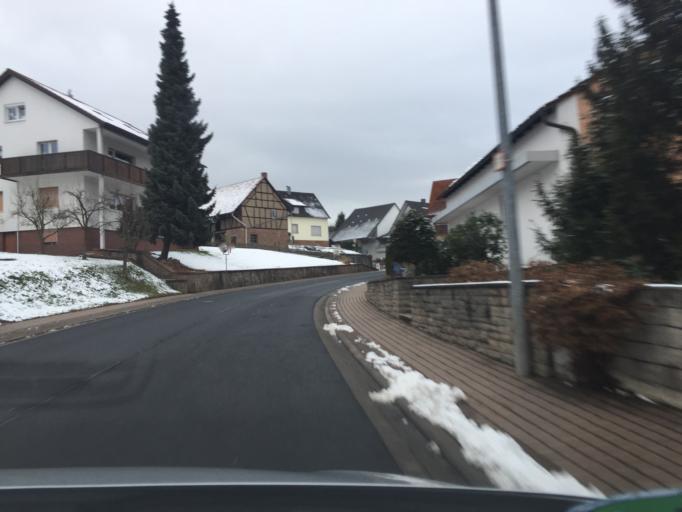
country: DE
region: Bavaria
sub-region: Regierungsbezirk Unterfranken
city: Krombach
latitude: 50.0988
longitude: 9.2301
